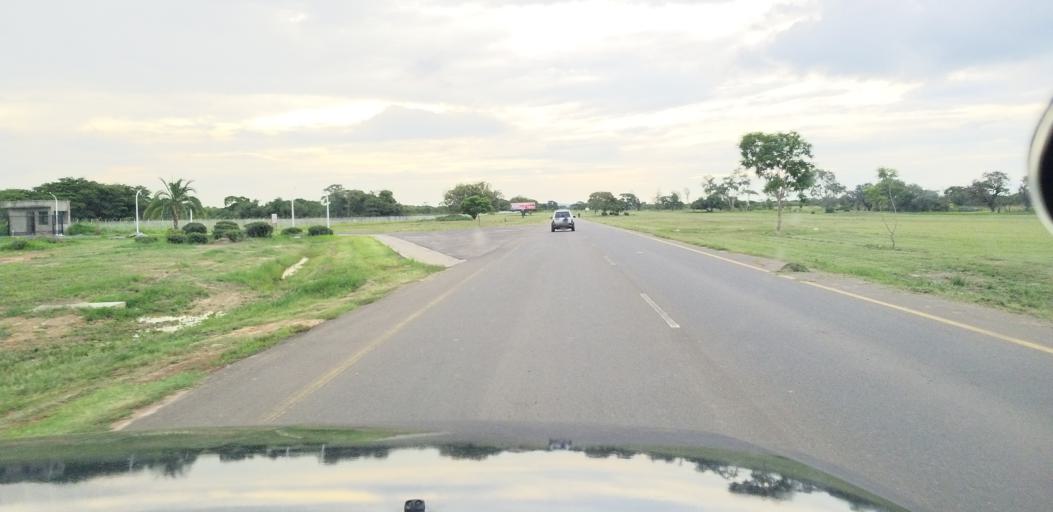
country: ZM
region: Lusaka
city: Lusaka
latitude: -15.3196
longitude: 28.4360
